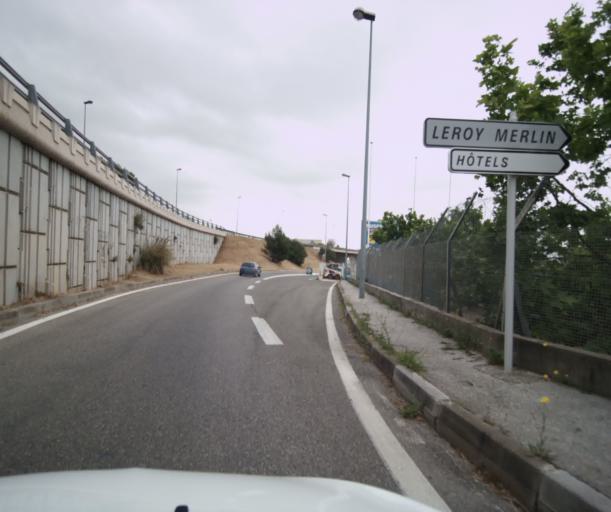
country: FR
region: Provence-Alpes-Cote d'Azur
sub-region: Departement du Var
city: La Garde
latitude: 43.1411
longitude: 6.0042
